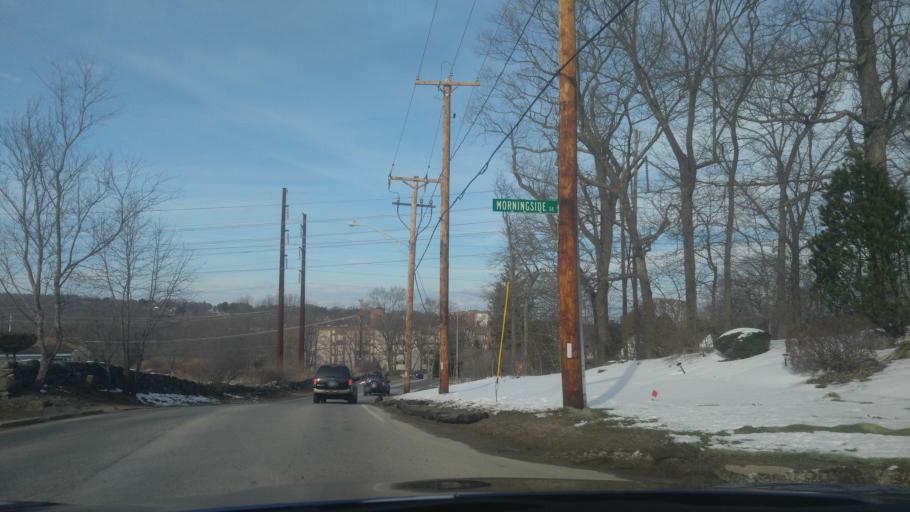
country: US
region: Rhode Island
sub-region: Kent County
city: West Warwick
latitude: 41.7102
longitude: -71.5063
